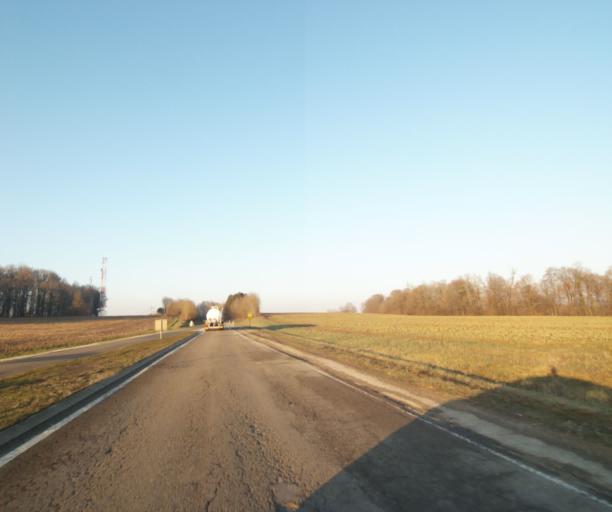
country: FR
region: Champagne-Ardenne
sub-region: Departement de la Haute-Marne
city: Bienville
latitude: 48.5734
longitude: 5.0354
